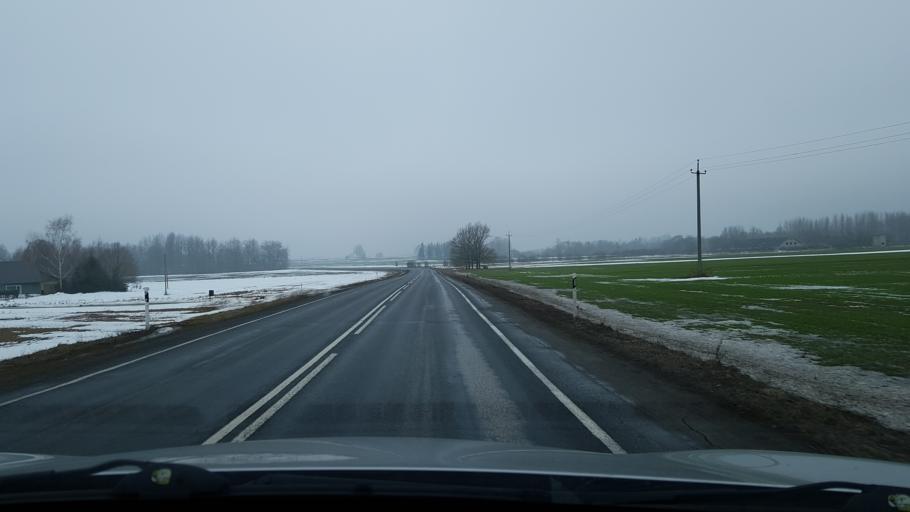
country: EE
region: Viljandimaa
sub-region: Viiratsi vald
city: Viiratsi
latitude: 58.2480
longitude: 25.8464
